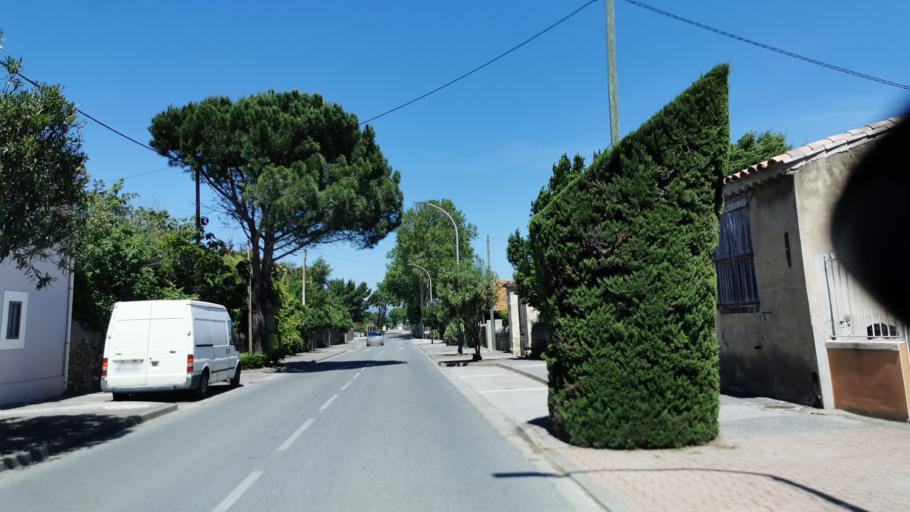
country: FR
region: Languedoc-Roussillon
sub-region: Departement de l'Aude
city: Saint-Marcel-sur-Aude
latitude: 43.2451
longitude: 2.9206
